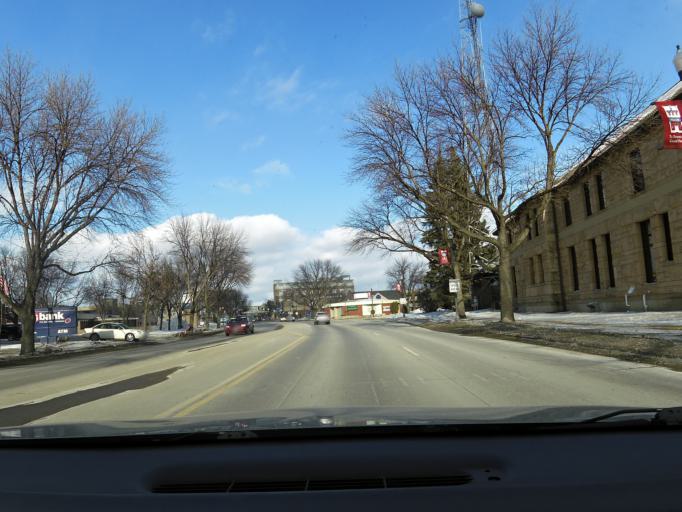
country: US
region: North Dakota
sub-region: Grand Forks County
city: Grand Forks
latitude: 47.9222
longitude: -97.0346
